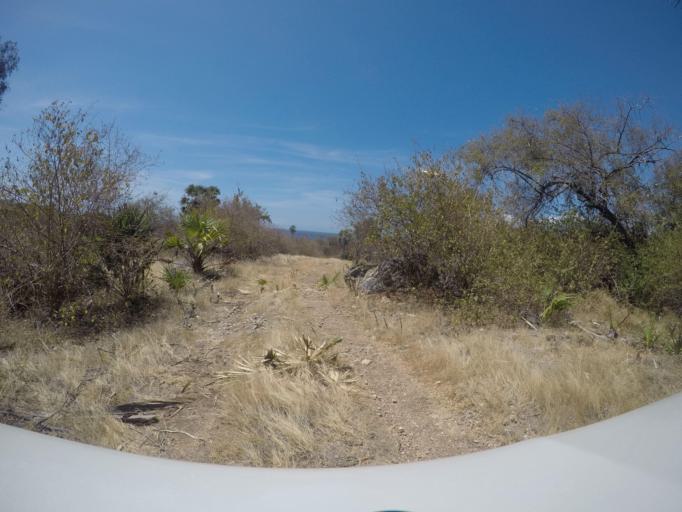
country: TL
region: Baucau
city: Baucau
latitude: -8.4349
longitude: 126.4402
